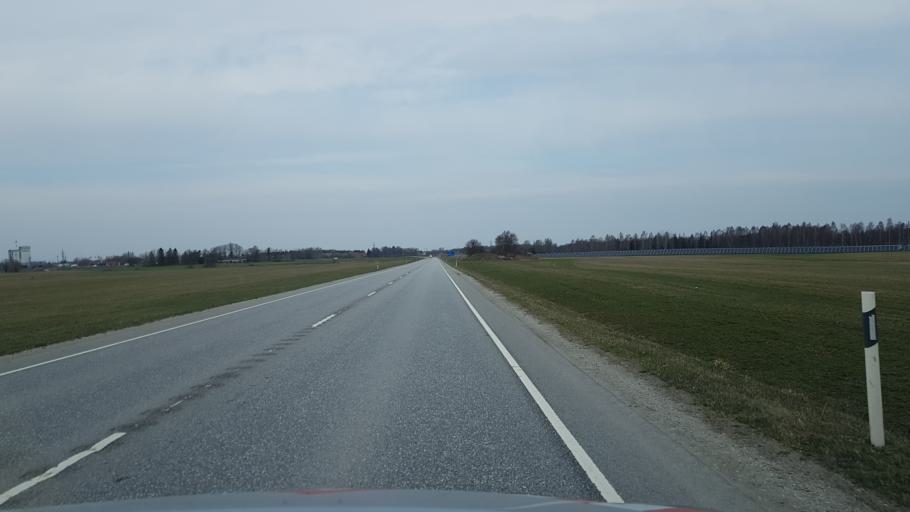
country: EE
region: Laeaene-Virumaa
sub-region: Someru vald
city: Someru
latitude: 59.3502
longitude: 26.4023
